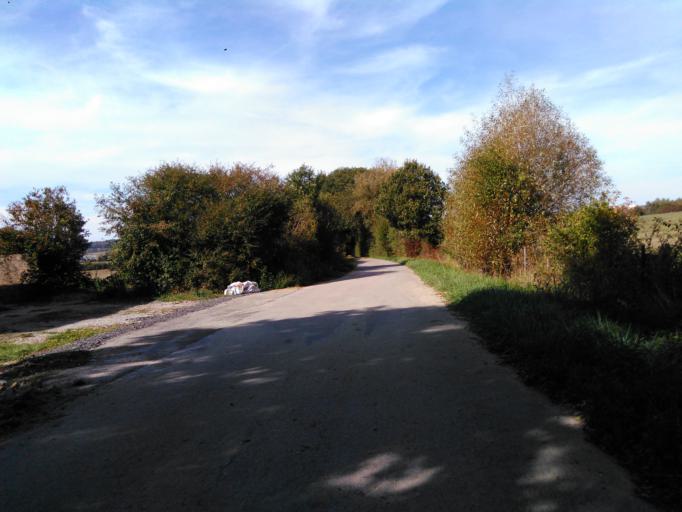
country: LU
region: Luxembourg
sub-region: Canton de Capellen
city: Bascharage
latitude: 49.5568
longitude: 5.9118
